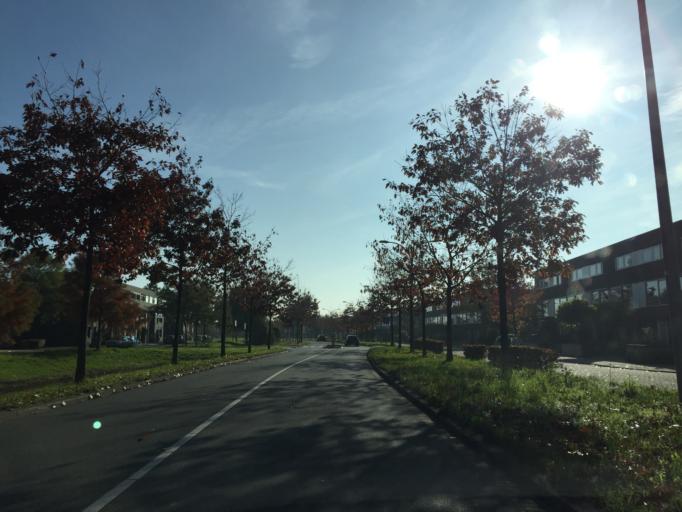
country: NL
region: South Holland
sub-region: Gemeente Delft
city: Delft
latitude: 52.0027
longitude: 4.3920
